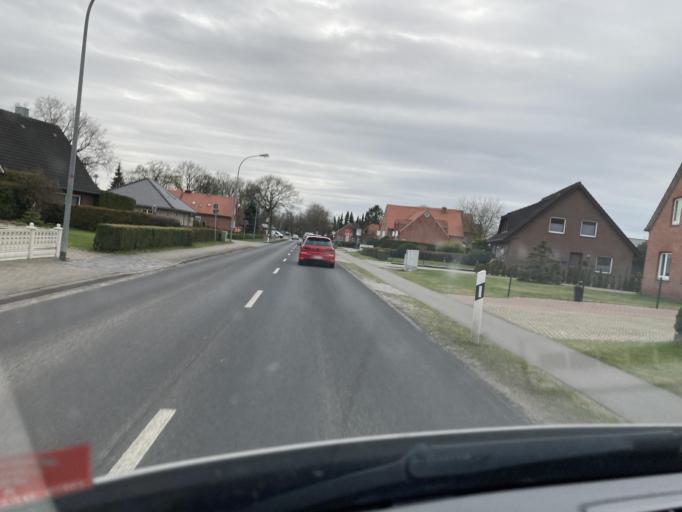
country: DE
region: Lower Saxony
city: Papenburg
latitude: 53.1257
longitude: 7.4630
